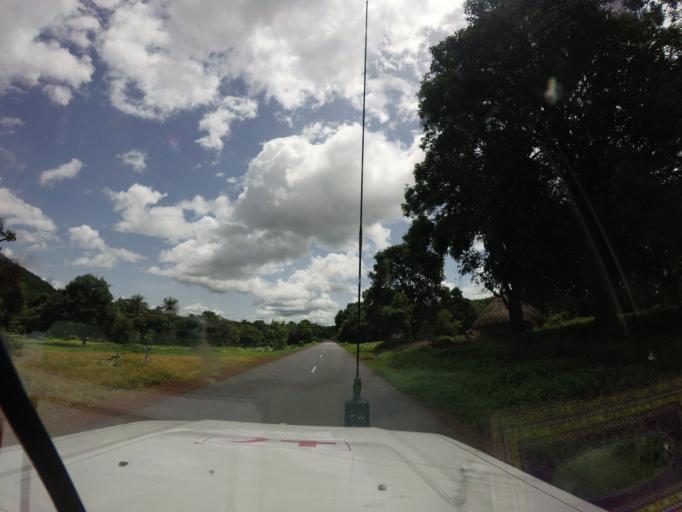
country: SL
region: Northern Province
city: Bindi
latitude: 10.1375
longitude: -11.6461
